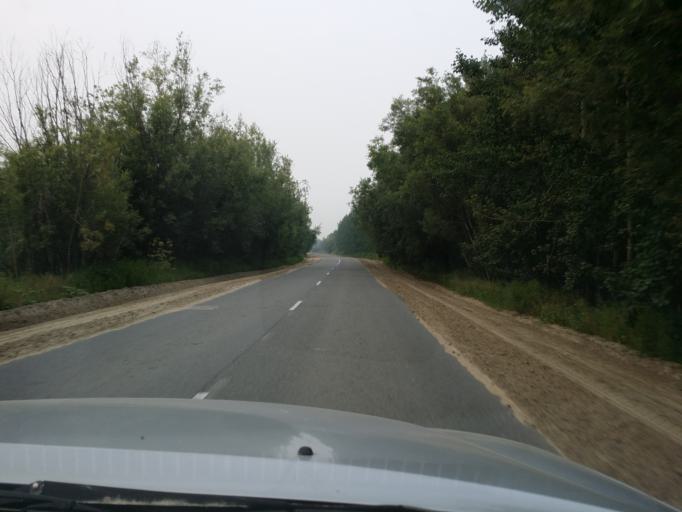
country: RU
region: Khanty-Mansiyskiy Avtonomnyy Okrug
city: Megion
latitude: 61.0044
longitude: 76.3087
